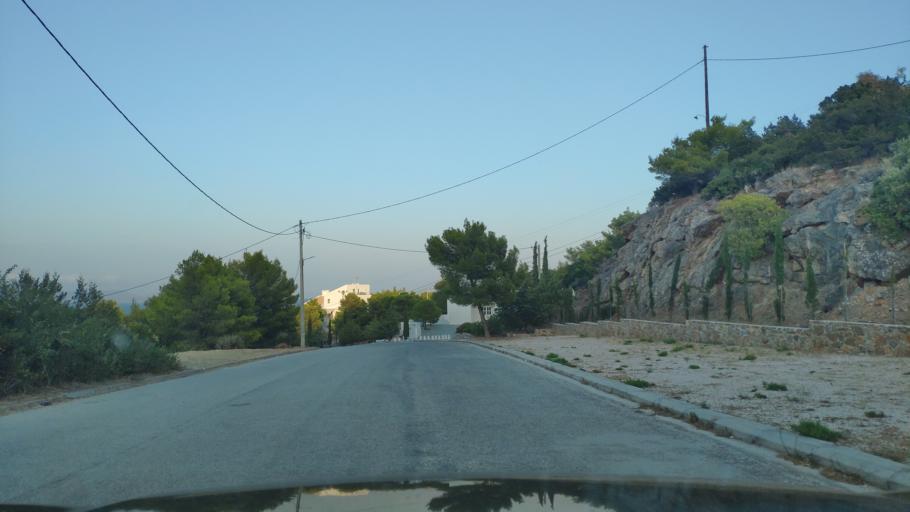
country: GR
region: Attica
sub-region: Nomarchia Anatolikis Attikis
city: Limin Mesoyaias
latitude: 37.9169
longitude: 24.0205
